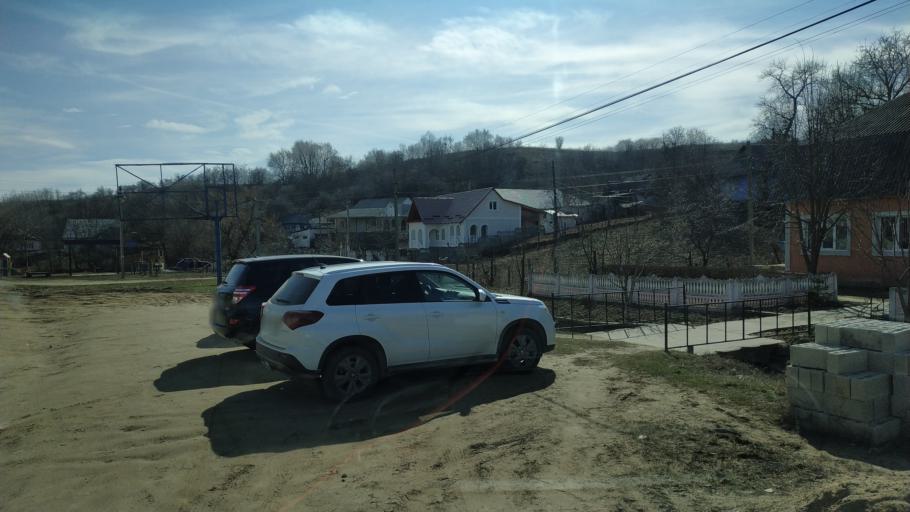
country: MD
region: Nisporeni
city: Nisporeni
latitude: 47.0950
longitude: 28.2991
